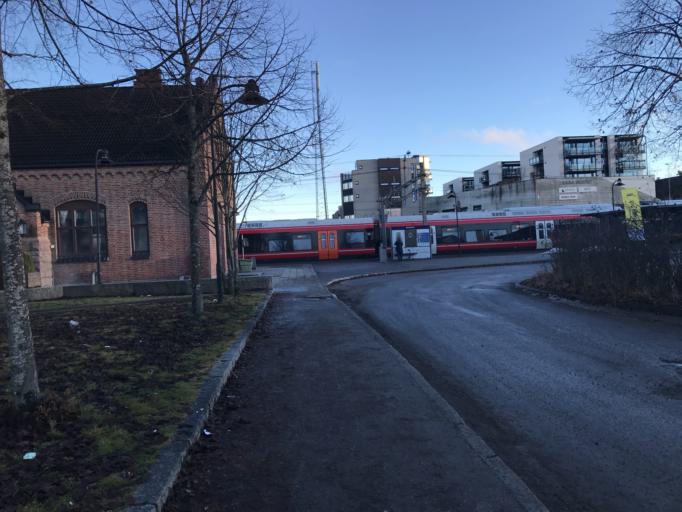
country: NO
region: Akershus
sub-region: Ullensaker
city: Jessheim
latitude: 60.1421
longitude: 11.1760
